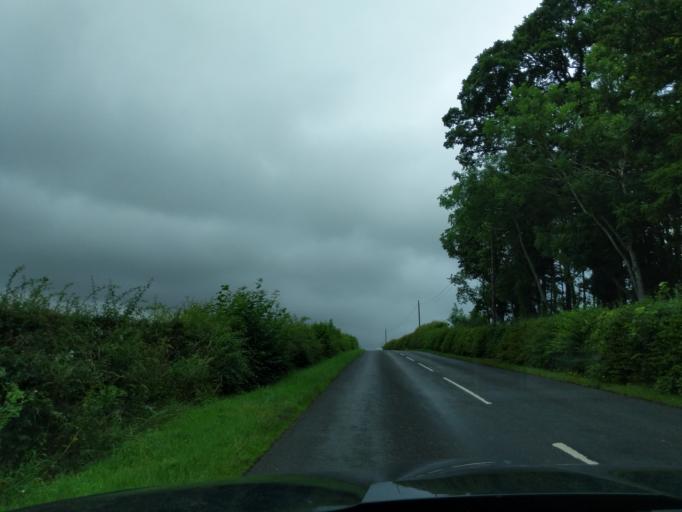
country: GB
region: England
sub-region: Northumberland
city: Ford
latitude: 55.6319
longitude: -2.0982
